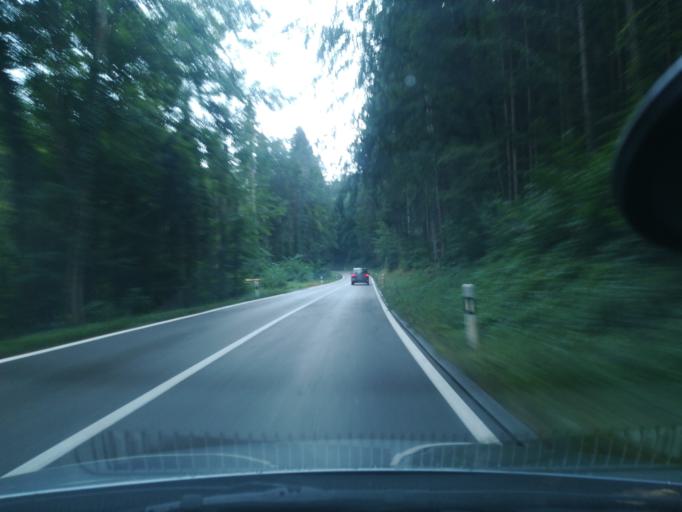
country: CH
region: Thurgau
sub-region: Frauenfeld District
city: Eschenz
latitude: 47.6338
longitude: 8.8742
